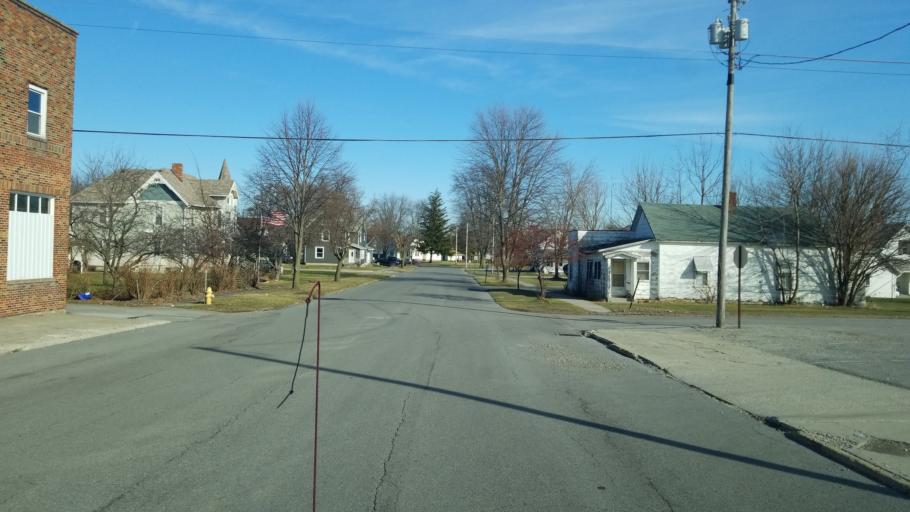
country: US
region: Ohio
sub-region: Putnam County
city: Leipsic
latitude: 41.0997
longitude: -83.9853
